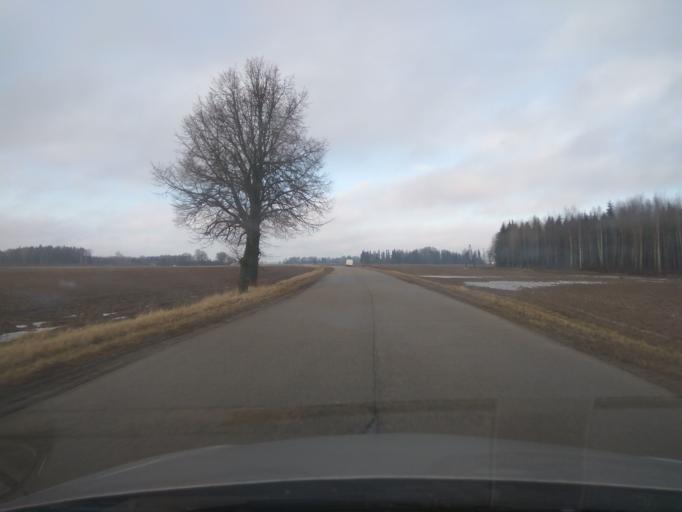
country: LV
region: Saldus Rajons
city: Saldus
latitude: 56.7855
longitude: 22.3880
